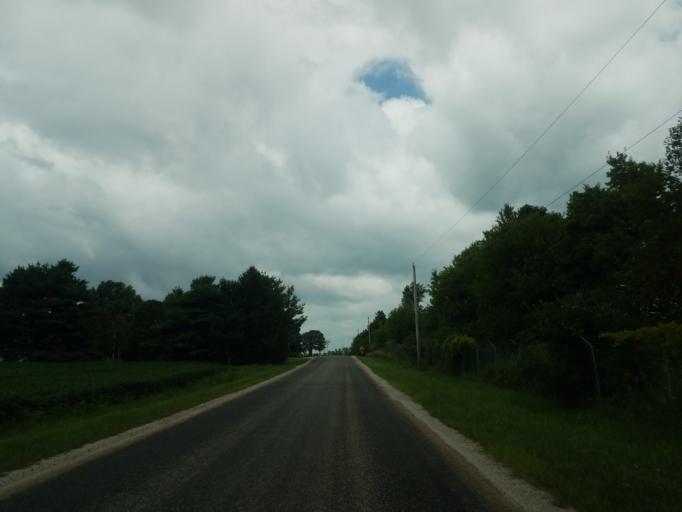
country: US
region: Illinois
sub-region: McLean County
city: Twin Grove
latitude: 40.4714
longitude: -89.0398
